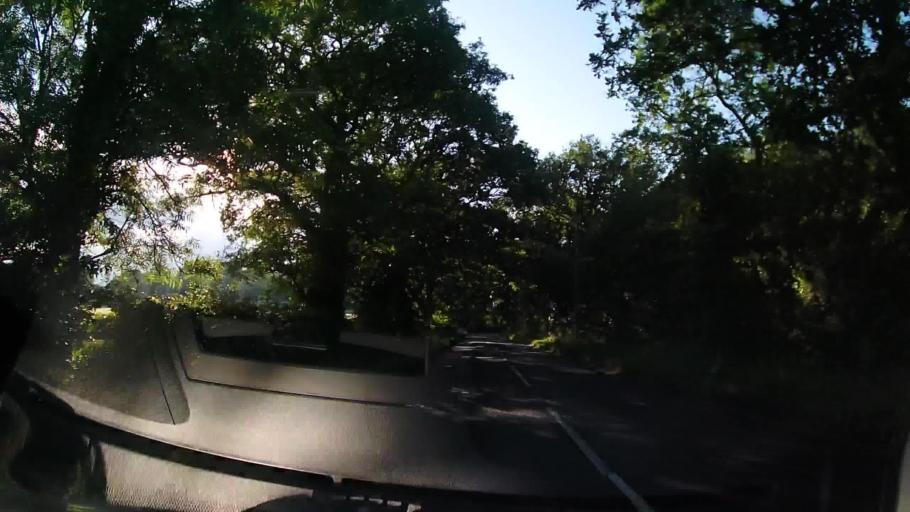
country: GB
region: England
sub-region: Leicestershire
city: Markfield
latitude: 52.6588
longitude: -1.2633
